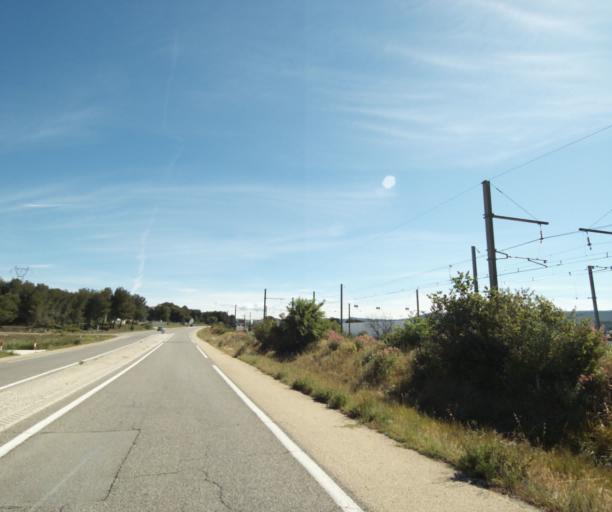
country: FR
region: Provence-Alpes-Cote d'Azur
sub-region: Departement des Bouches-du-Rhone
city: Rognac
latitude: 43.4989
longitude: 5.2079
